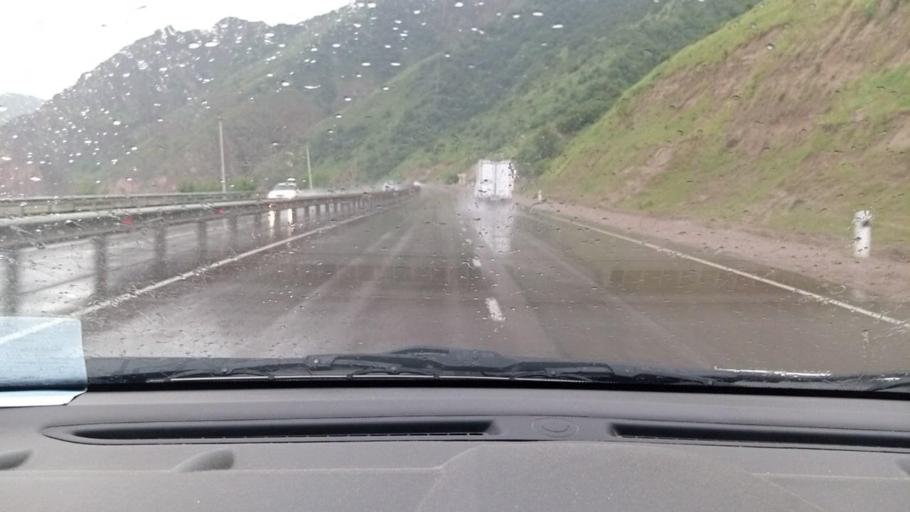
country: UZ
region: Toshkent
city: Angren
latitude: 41.0943
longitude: 70.3207
